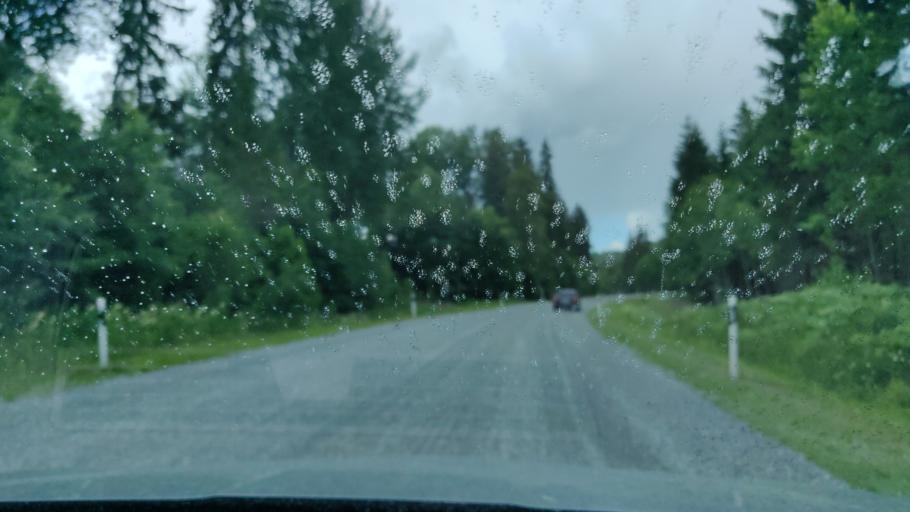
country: EE
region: Vorumaa
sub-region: Antsla vald
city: Vana-Antsla
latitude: 58.0308
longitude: 26.5711
